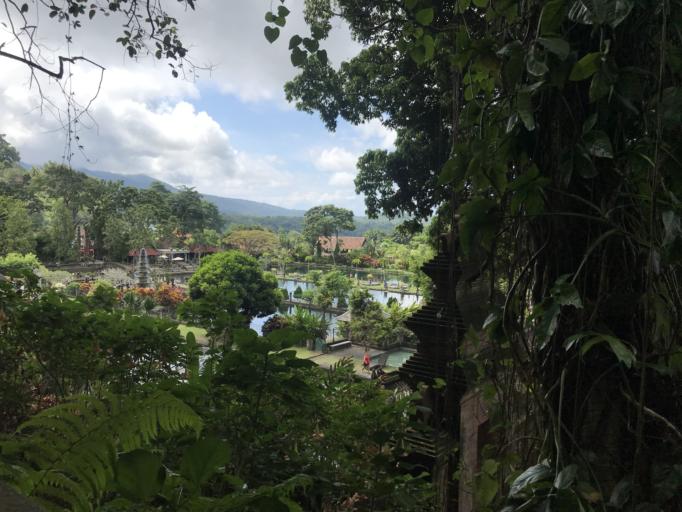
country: ID
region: Bali
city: Banjar Ababi
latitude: -8.4124
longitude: 115.5861
